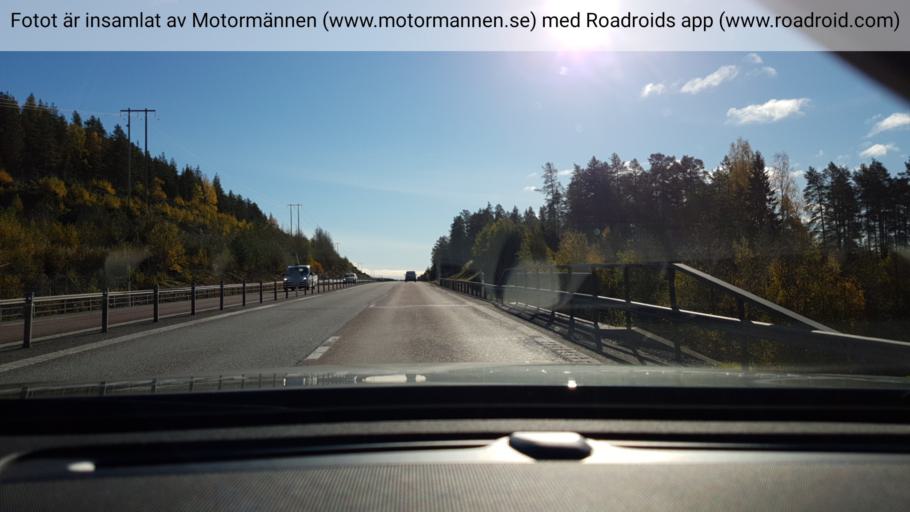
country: SE
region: Vaesterbotten
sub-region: Skelleftea Kommun
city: Soedra Bergsbyn
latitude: 64.6580
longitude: 21.1153
